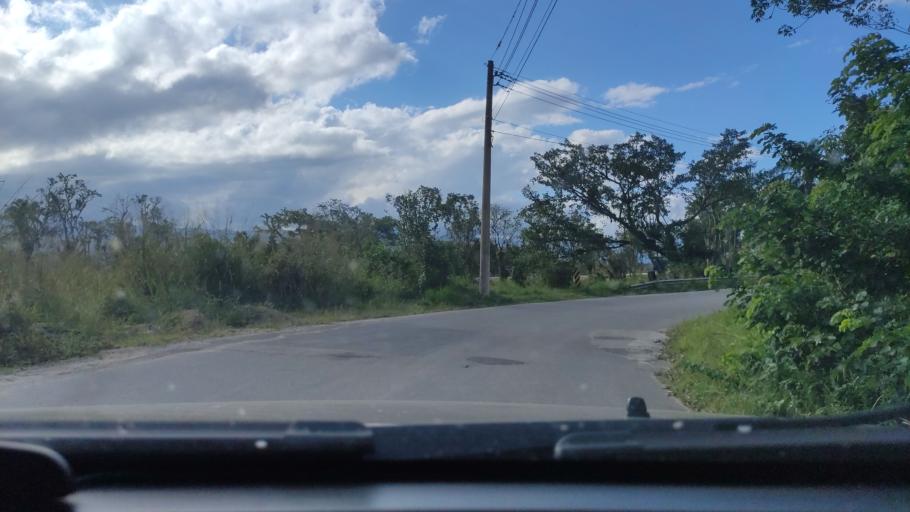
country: BR
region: Sao Paulo
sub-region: Sao Sebastiao
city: Sao Sebastiao
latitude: -23.6949
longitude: -45.4628
